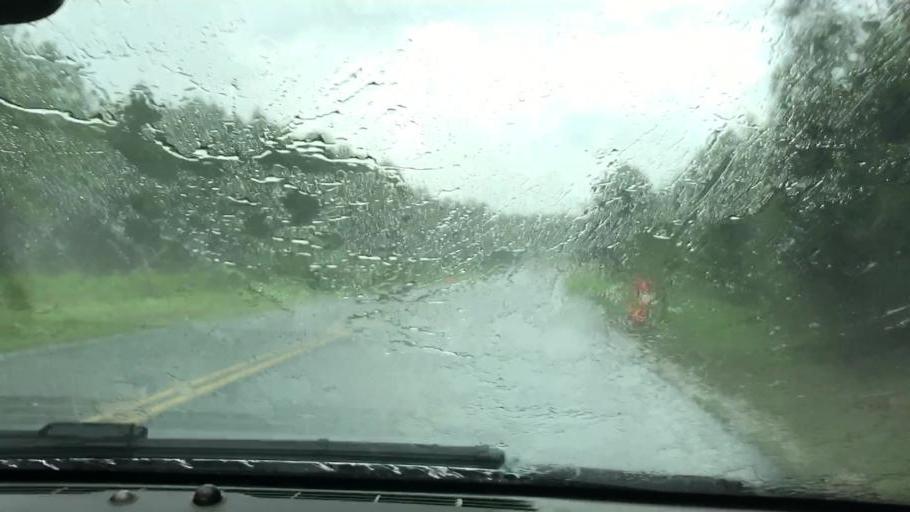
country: US
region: Georgia
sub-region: Clay County
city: Fort Gaines
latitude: 31.5600
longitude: -85.0224
